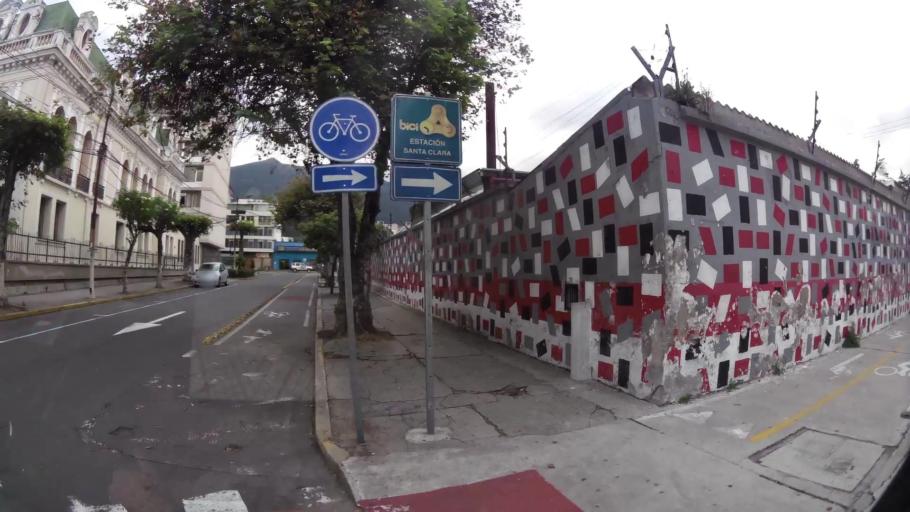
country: EC
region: Pichincha
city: Quito
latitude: -0.2027
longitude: -78.4971
